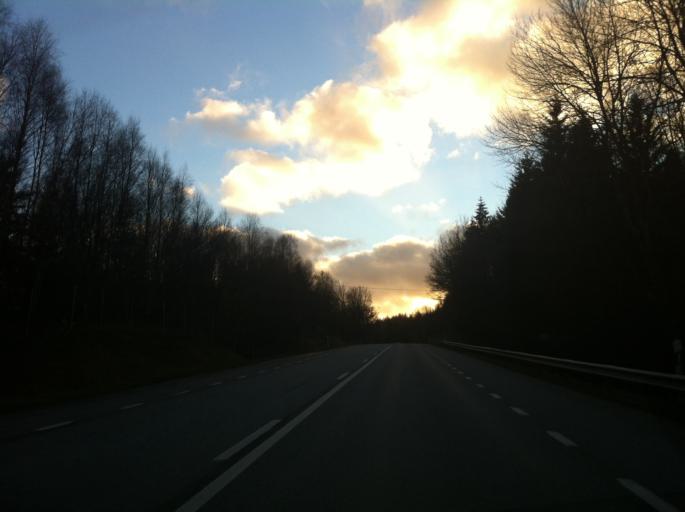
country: SE
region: Skane
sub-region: Hassleholms Kommun
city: Sosdala
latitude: 56.0049
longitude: 13.6490
